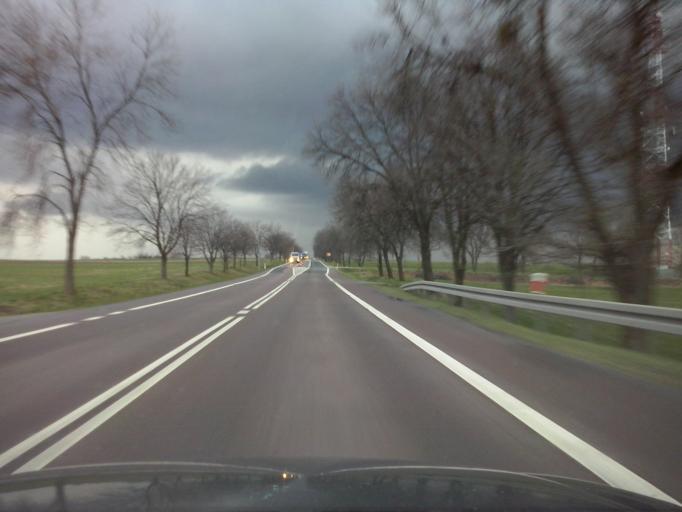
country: PL
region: Lublin Voivodeship
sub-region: Powiat chelmski
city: Rejowiec Fabryczny
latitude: 51.1775
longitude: 23.2236
